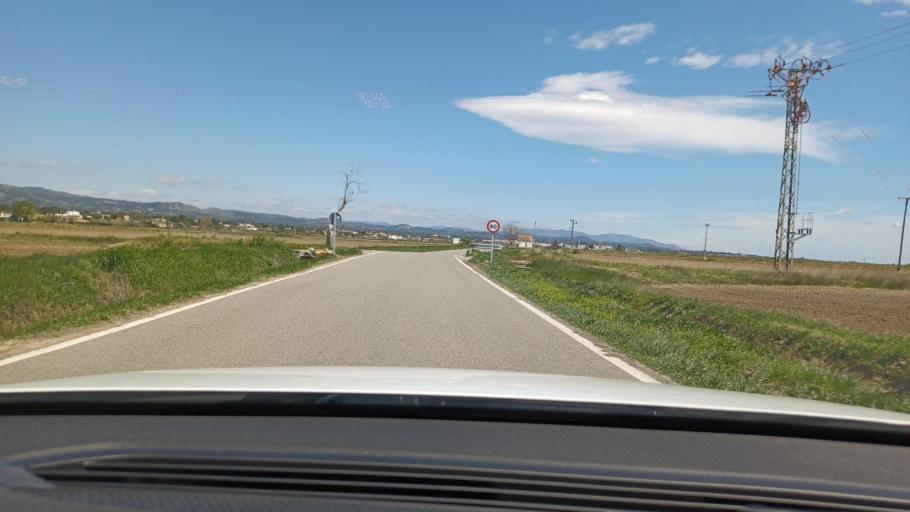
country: ES
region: Catalonia
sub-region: Provincia de Tarragona
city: Camarles
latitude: 40.7813
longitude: 0.6906
